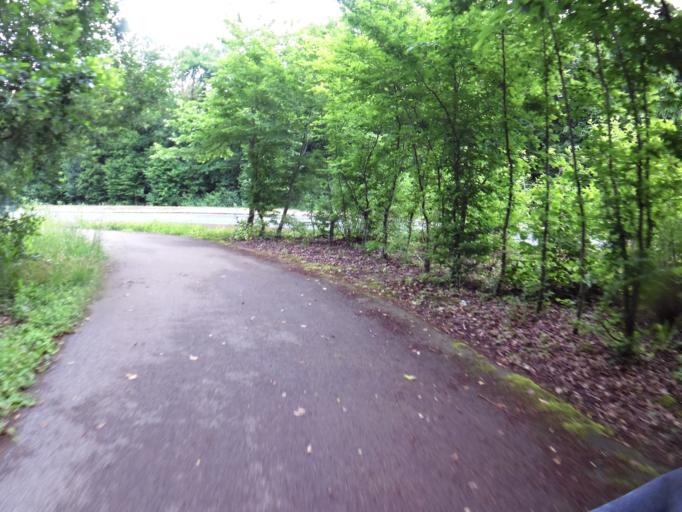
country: FR
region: Champagne-Ardenne
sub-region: Departement de la Haute-Marne
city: Laneuville-a-Remy
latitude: 48.5723
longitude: 4.8491
